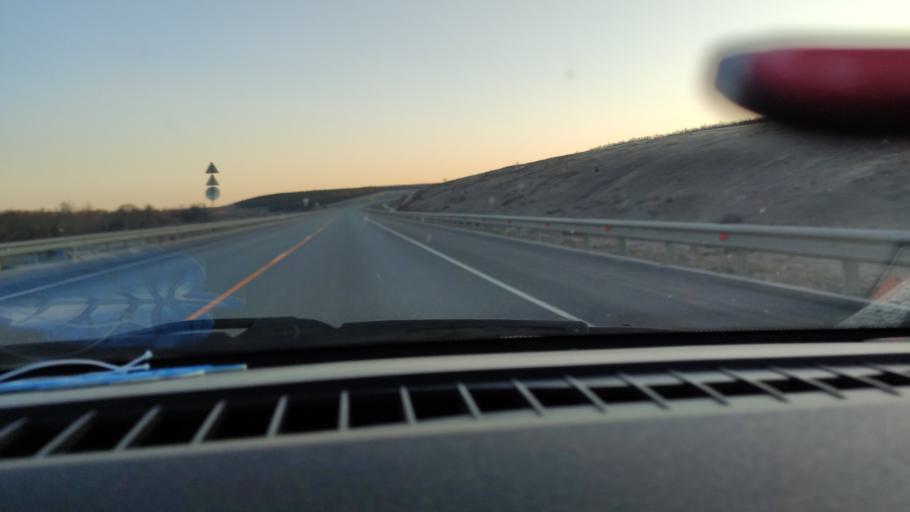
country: RU
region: Saratov
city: Yelshanka
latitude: 51.8693
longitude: 46.5033
